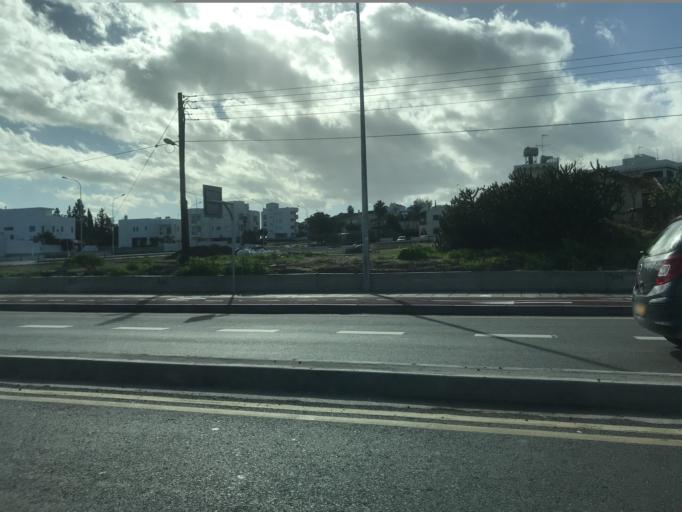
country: CY
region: Lefkosia
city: Nicosia
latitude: 35.1523
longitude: 33.4049
